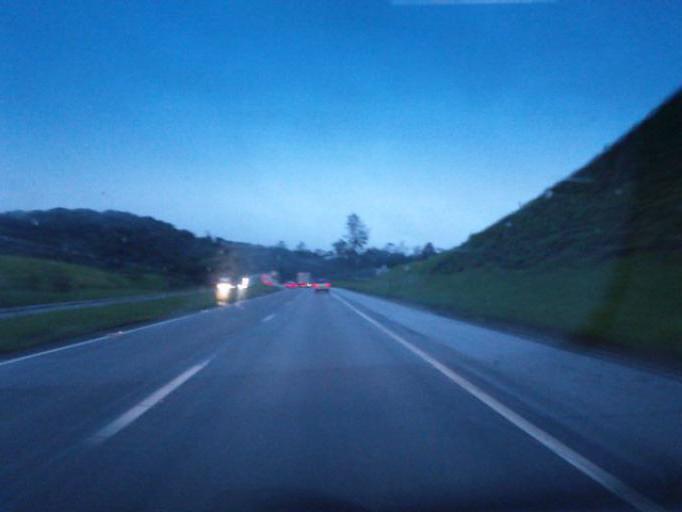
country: BR
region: Sao Paulo
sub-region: Juquitiba
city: Juquitiba
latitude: -23.9422
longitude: -47.0935
